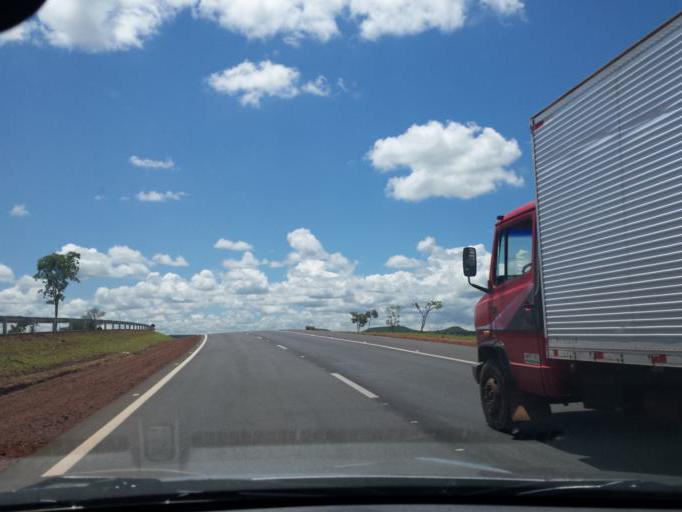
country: BR
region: Goias
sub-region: Cristalina
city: Cristalina
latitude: -16.6025
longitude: -47.7719
